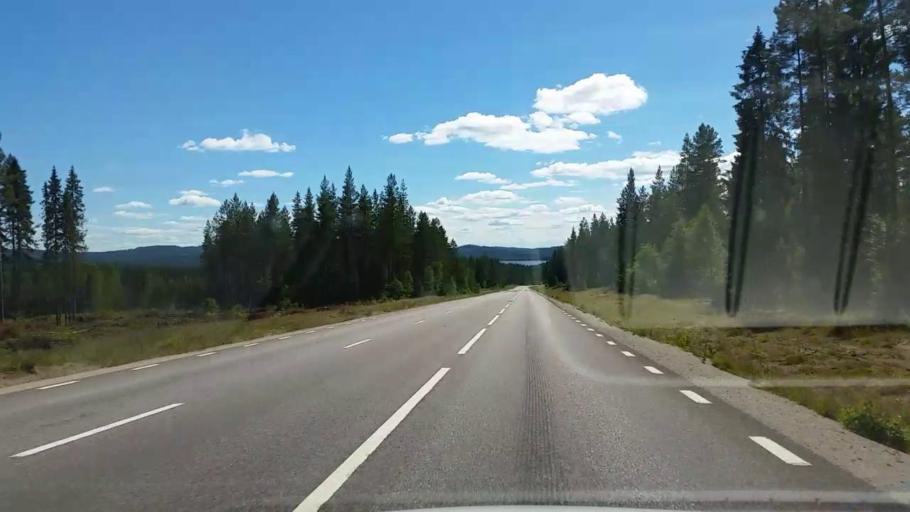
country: SE
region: Gaevleborg
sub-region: Bollnas Kommun
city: Vittsjo
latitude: 61.0569
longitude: 15.8030
